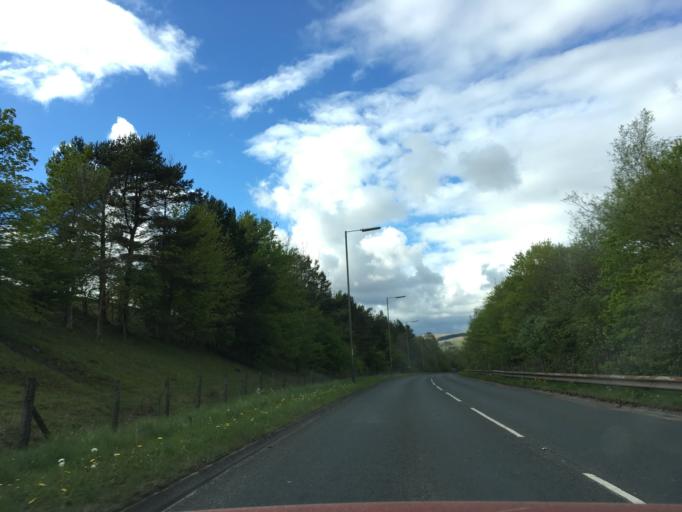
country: GB
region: Wales
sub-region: Caerphilly County Borough
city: Rhymney
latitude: 51.7570
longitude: -3.2904
